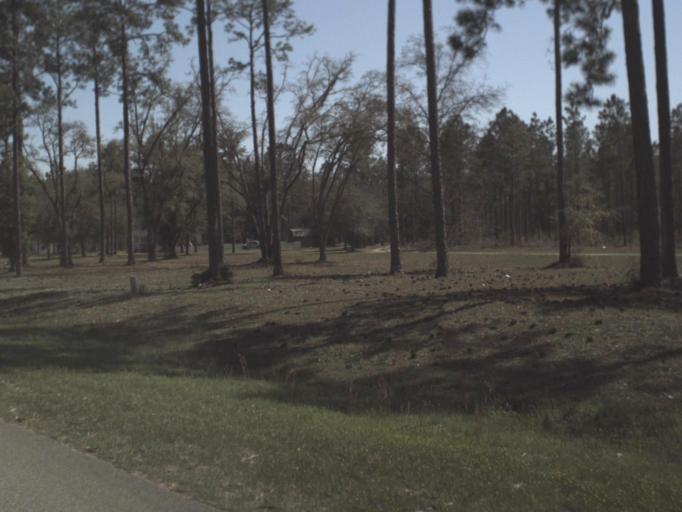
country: US
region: Florida
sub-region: Liberty County
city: Bristol
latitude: 30.4027
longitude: -84.8173
